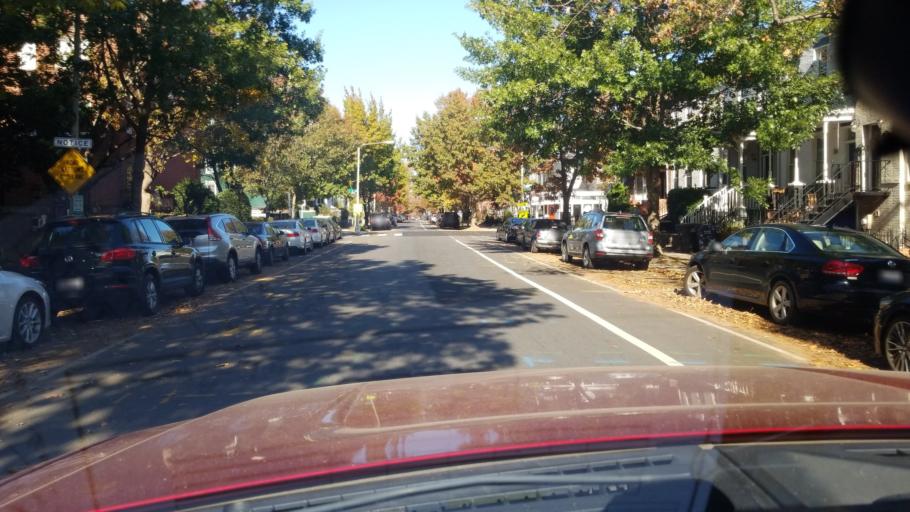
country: US
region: Washington, D.C.
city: Washington, D.C.
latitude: 38.8904
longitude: -76.9837
